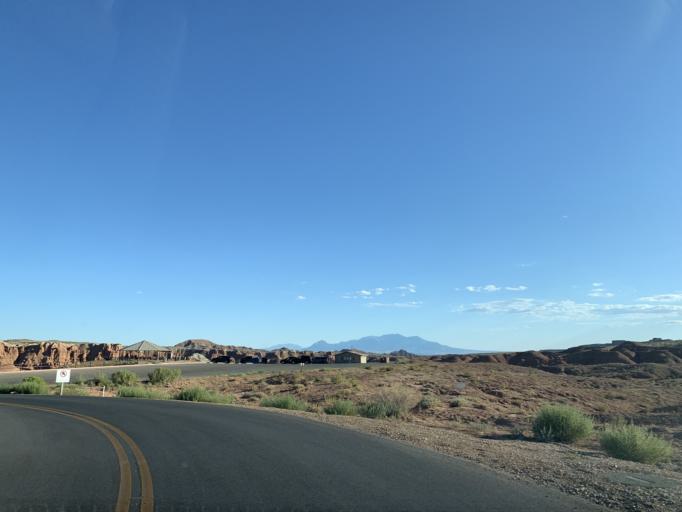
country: US
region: Utah
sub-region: Emery County
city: Ferron
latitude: 38.5654
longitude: -110.7036
